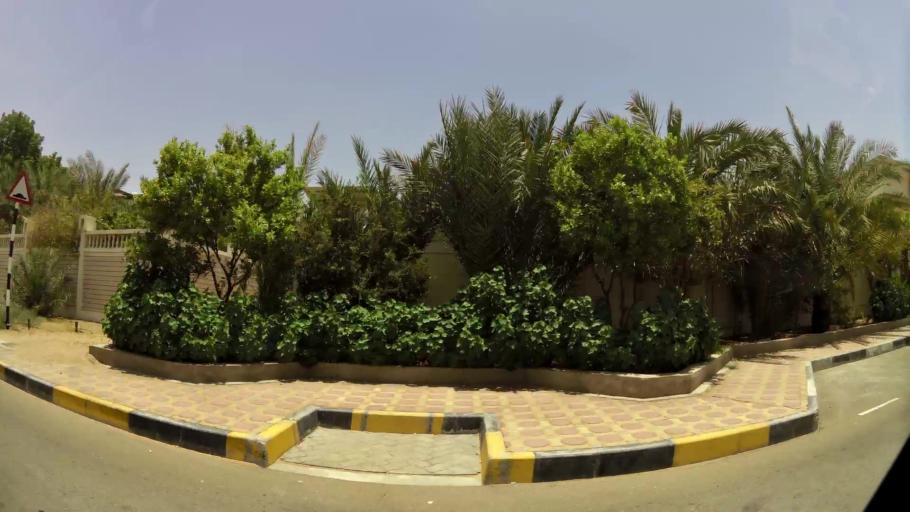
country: OM
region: Al Buraimi
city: Al Buraymi
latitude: 24.2673
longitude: 55.7244
